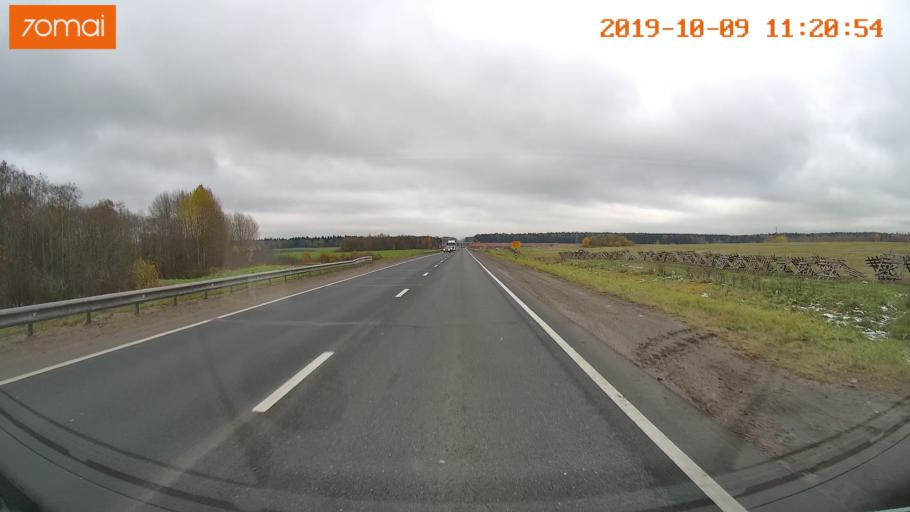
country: RU
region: Vologda
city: Vologda
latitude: 59.1445
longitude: 39.9440
